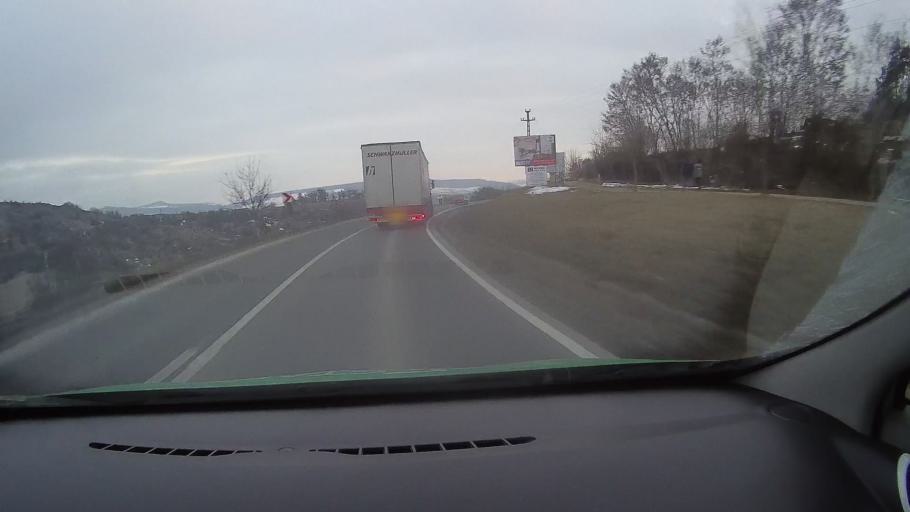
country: RO
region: Harghita
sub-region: Municipiul Odorheiu Secuiesc
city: Odorheiu Secuiesc
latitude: 46.3248
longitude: 25.2797
